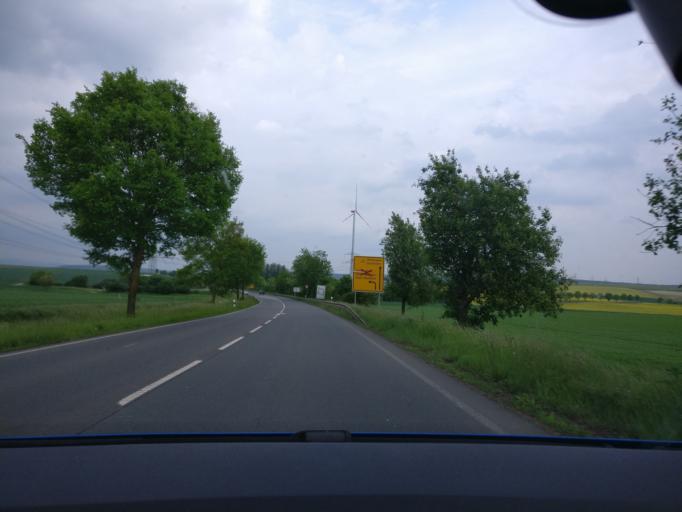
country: DE
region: Rheinland-Pfalz
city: Netzbach
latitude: 50.3403
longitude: 8.1234
